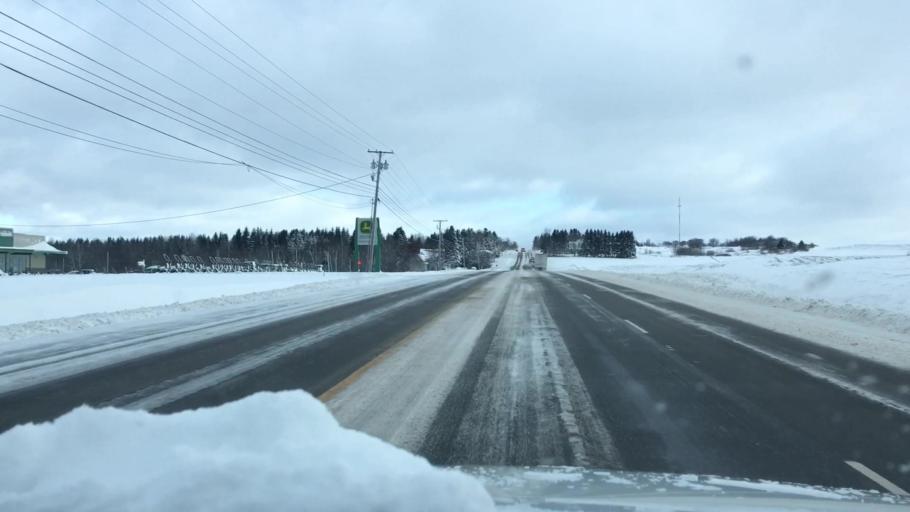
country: US
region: Maine
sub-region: Aroostook County
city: Presque Isle
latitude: 46.7194
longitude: -68.0072
